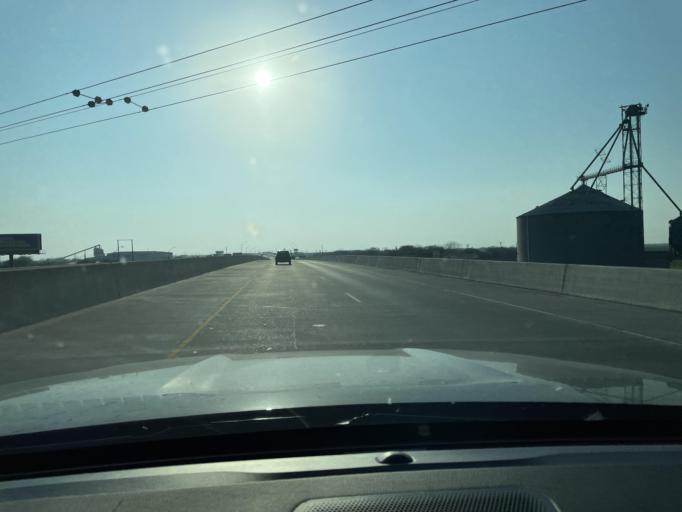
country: US
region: Texas
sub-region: Nueces County
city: Robstown
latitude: 27.7760
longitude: -97.6678
